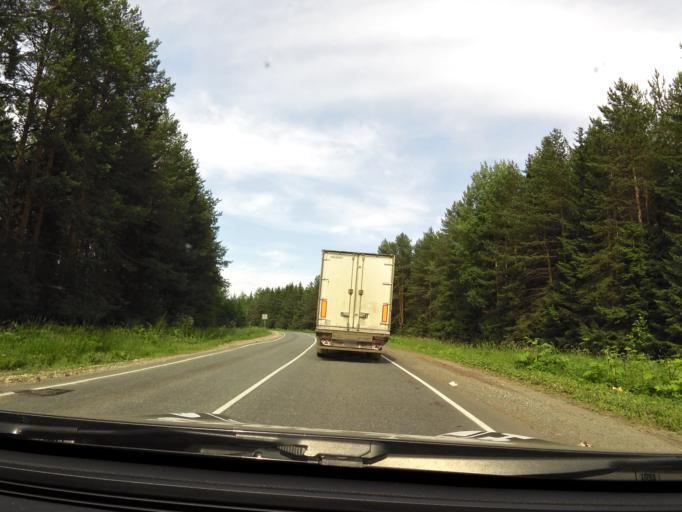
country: RU
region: Kirov
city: Slobodskoy
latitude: 58.7576
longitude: 50.3283
